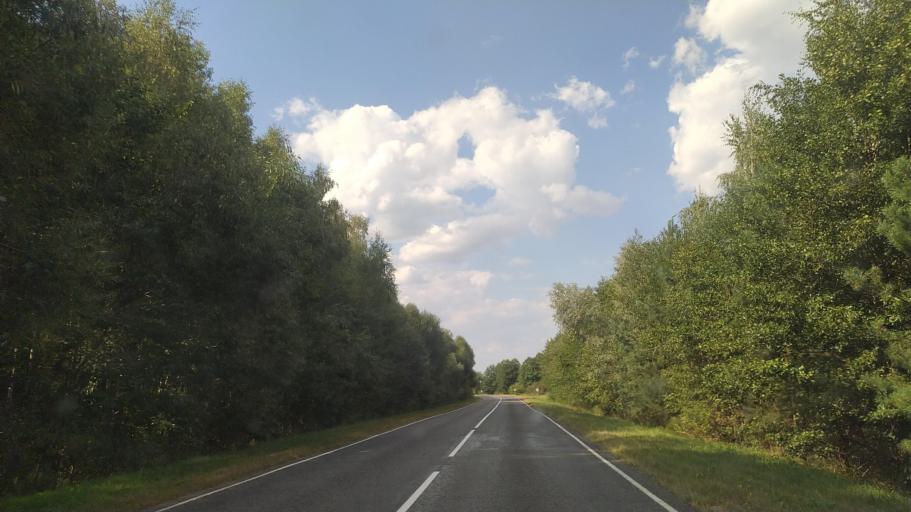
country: BY
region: Brest
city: Drahichyn
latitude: 52.2345
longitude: 25.1120
